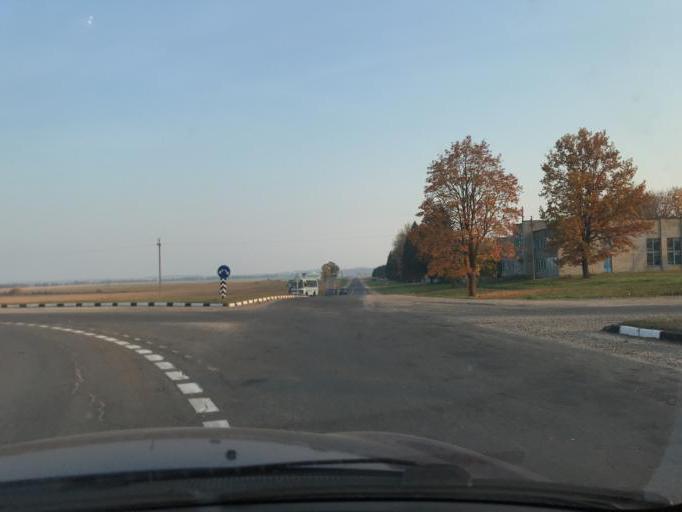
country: BY
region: Grodnenskaya
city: Karelichy
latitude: 53.5579
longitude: 26.1530
